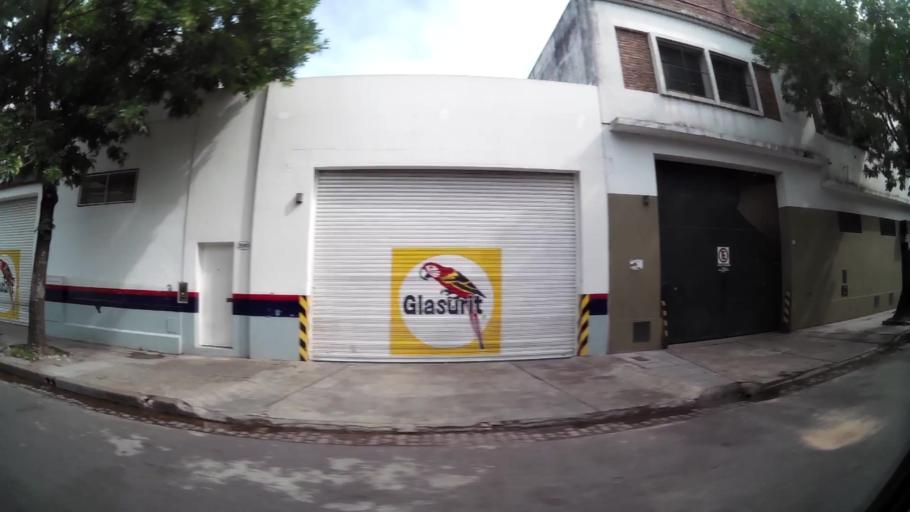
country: AR
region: Buenos Aires F.D.
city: Buenos Aires
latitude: -34.6398
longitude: -58.4131
